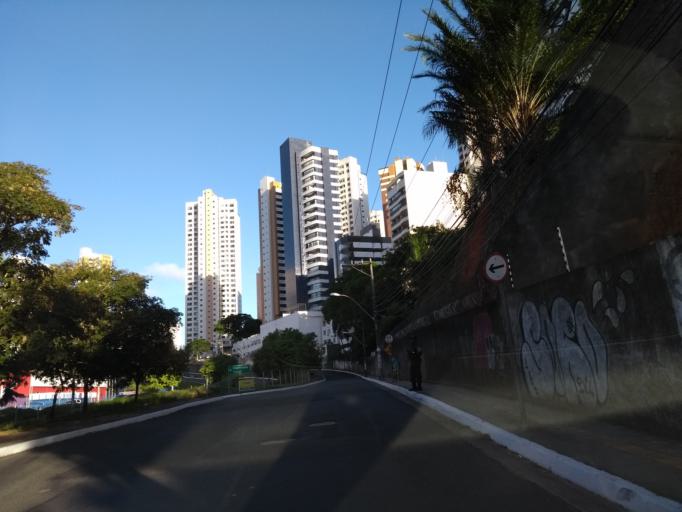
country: BR
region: Bahia
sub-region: Salvador
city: Salvador
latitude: -12.9998
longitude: -38.4910
